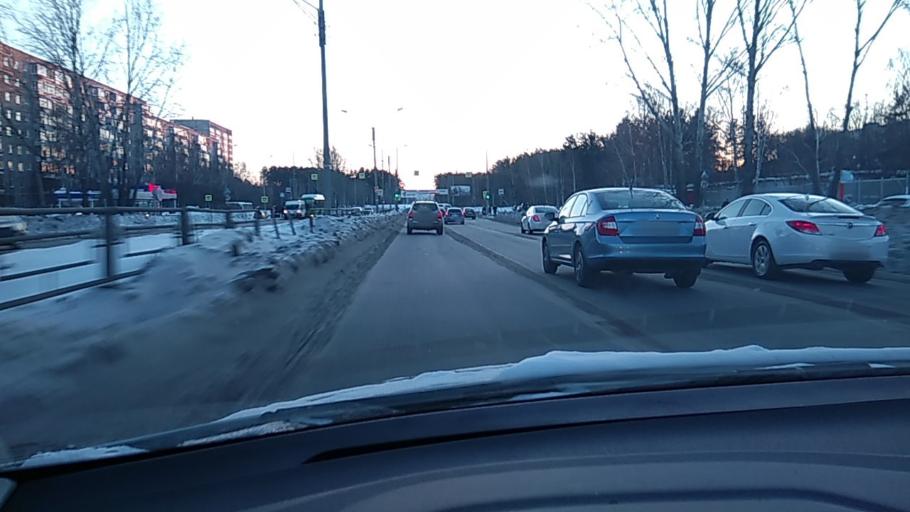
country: RU
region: Sverdlovsk
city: Sovkhoznyy
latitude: 56.8082
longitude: 60.5439
